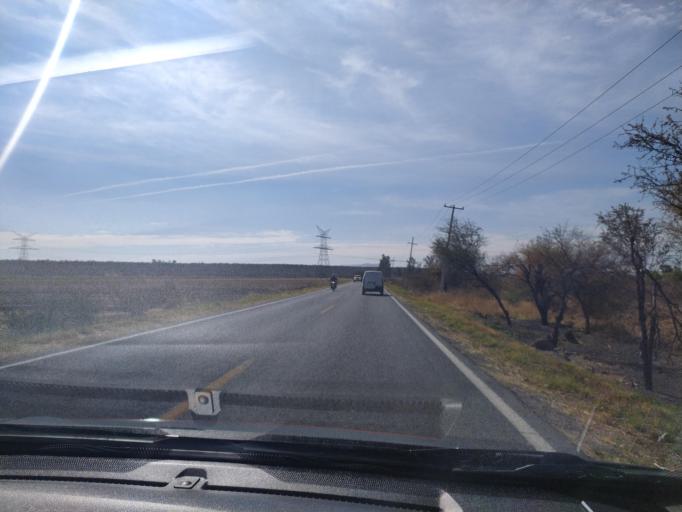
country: MX
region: Guanajuato
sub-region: San Francisco del Rincon
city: San Ignacio de Hidalgo
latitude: 20.9357
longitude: -101.8539
